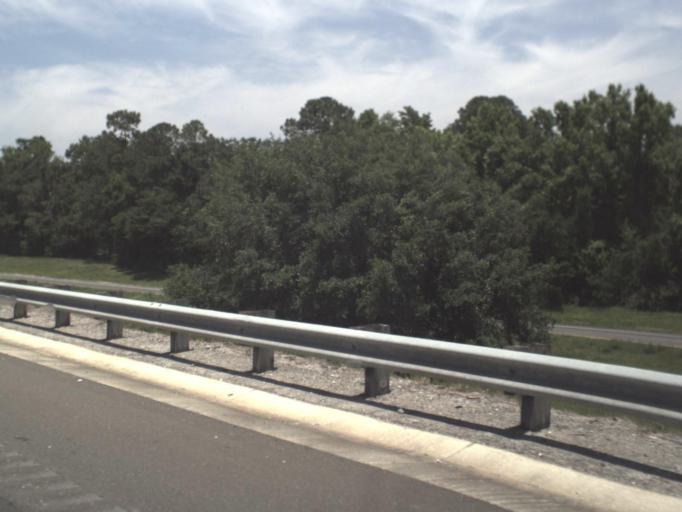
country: US
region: Florida
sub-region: Duval County
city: Jacksonville
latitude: 30.4488
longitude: -81.6139
